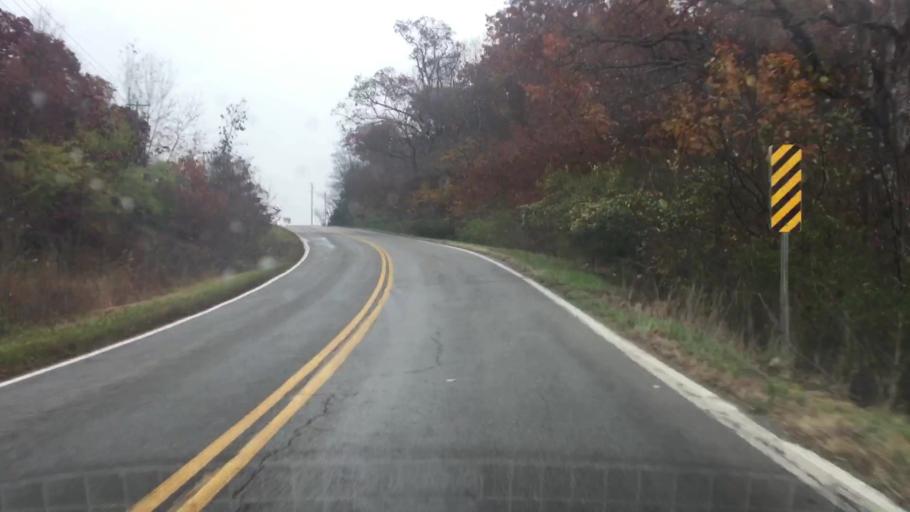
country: US
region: Missouri
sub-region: Callaway County
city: Fulton
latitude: 38.8416
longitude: -91.9257
